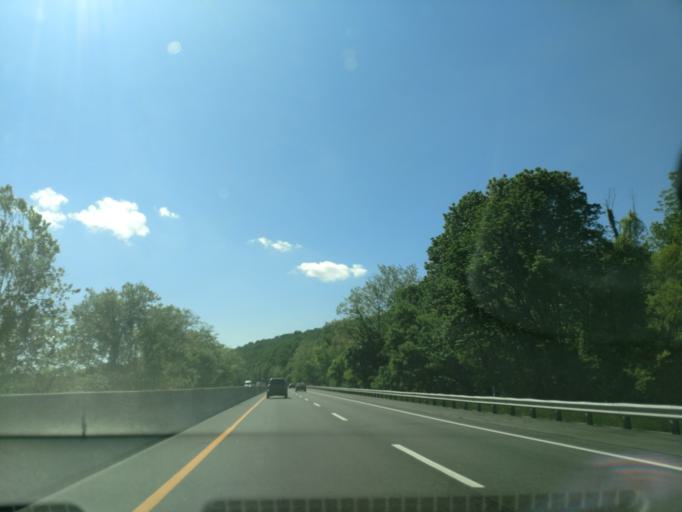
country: US
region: Pennsylvania
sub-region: Chester County
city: Chesterbrook
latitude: 40.0762
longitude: -75.4943
